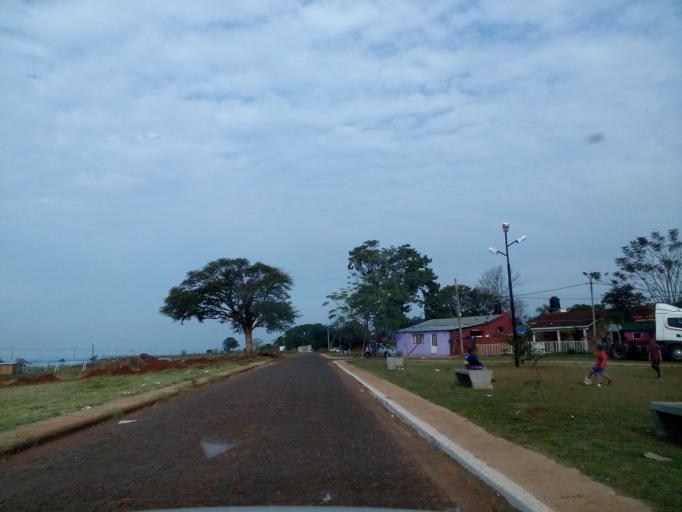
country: AR
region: Misiones
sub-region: Departamento de Capital
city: Posadas
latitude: -27.4196
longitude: -55.8822
